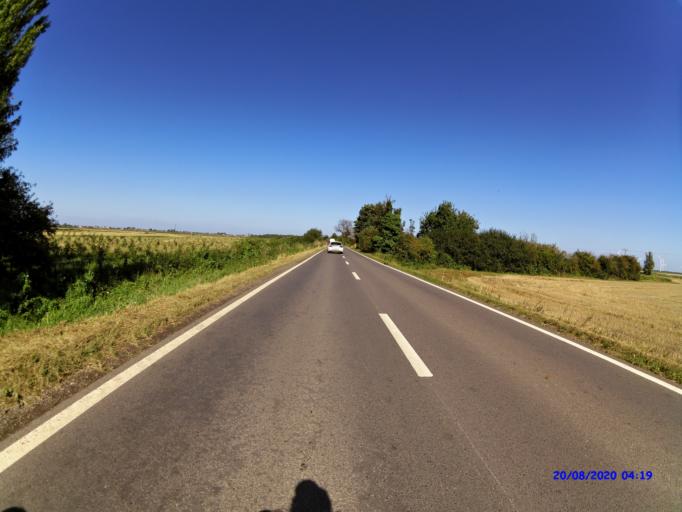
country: GB
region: England
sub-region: Cambridgeshire
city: Ramsey
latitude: 52.4922
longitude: -0.1183
